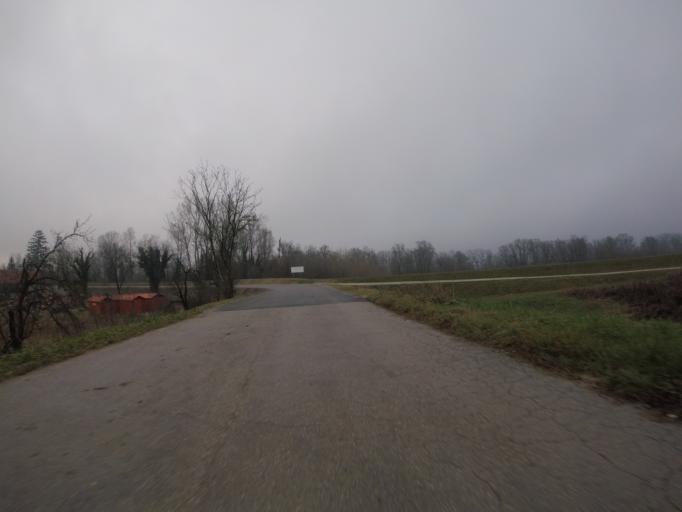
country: HR
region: Zagrebacka
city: Kuce
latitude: 45.7111
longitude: 16.2208
